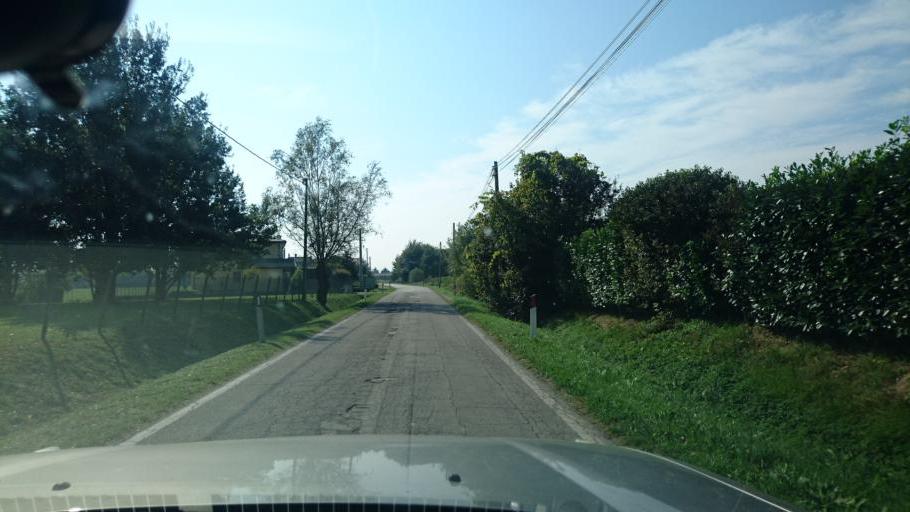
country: IT
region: Veneto
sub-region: Provincia di Padova
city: Rubano
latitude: 45.4086
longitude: 11.7968
